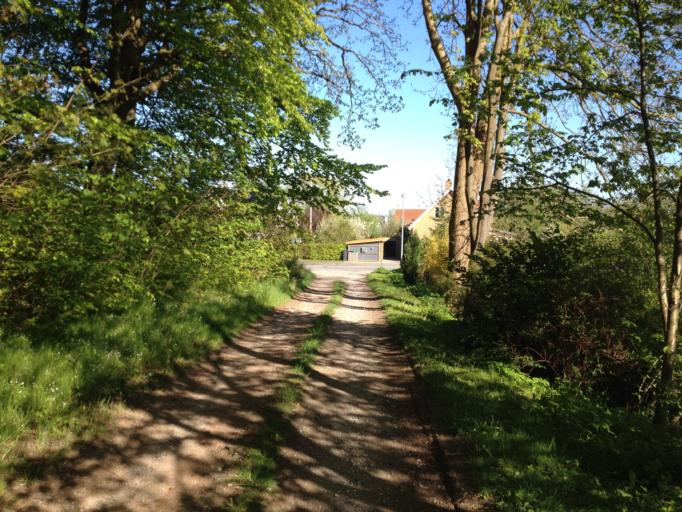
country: DK
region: Capital Region
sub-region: Fredensborg Kommune
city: Niva
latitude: 55.9409
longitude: 12.5204
